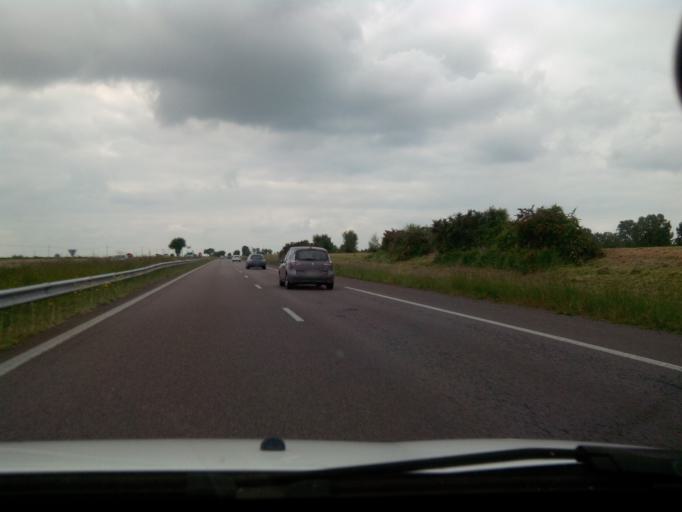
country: FR
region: Brittany
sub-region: Departement d'Ille-et-Vilaine
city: Bedee
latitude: 48.1868
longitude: -1.9612
